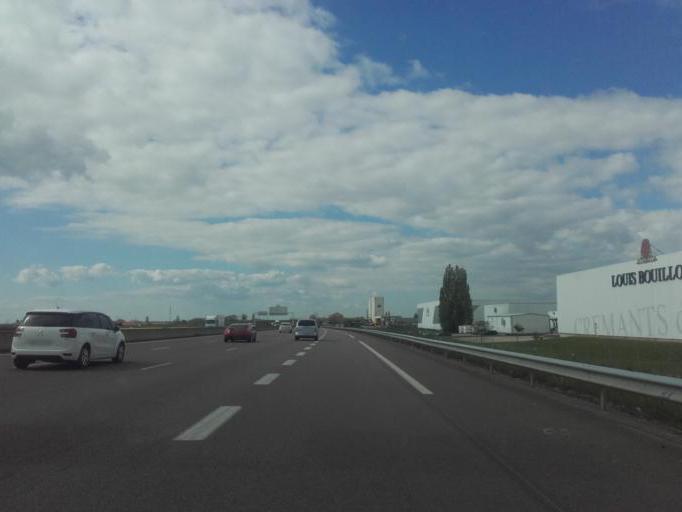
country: FR
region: Bourgogne
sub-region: Departement de la Cote-d'Or
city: Nuits-Saint-Georges
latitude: 47.1275
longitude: 4.9696
